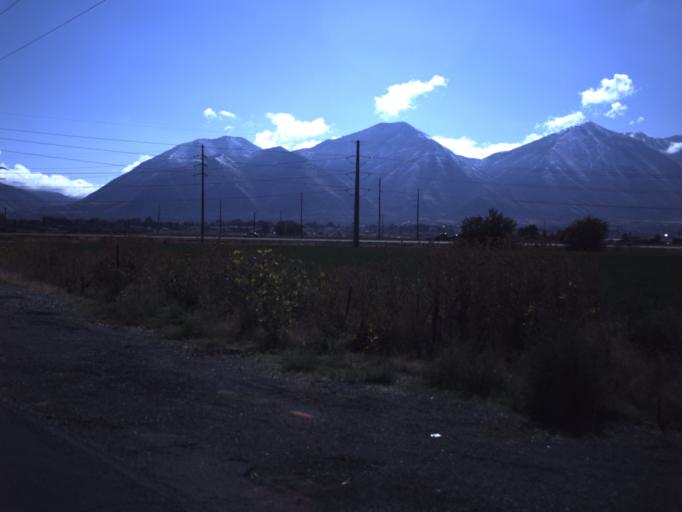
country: US
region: Utah
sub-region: Utah County
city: Benjamin
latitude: 40.0983
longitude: -111.6921
